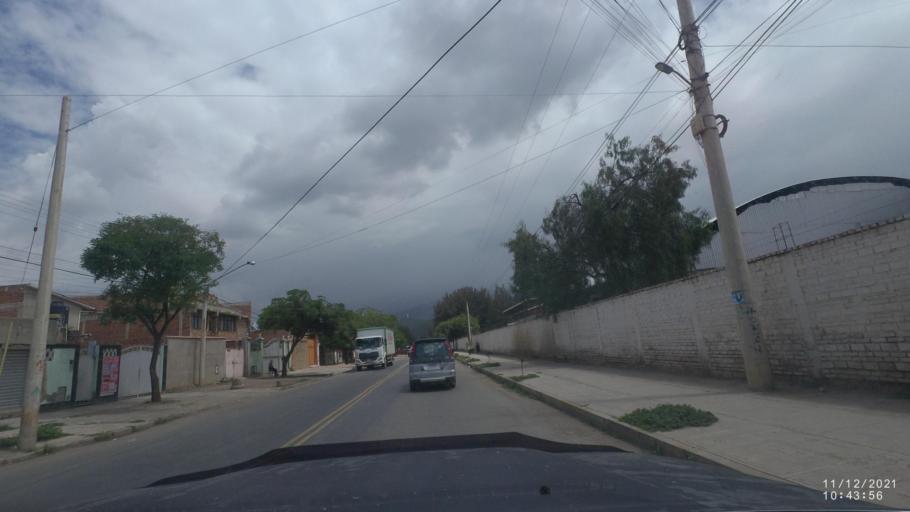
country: BO
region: Cochabamba
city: Cochabamba
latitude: -17.4200
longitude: -66.1312
